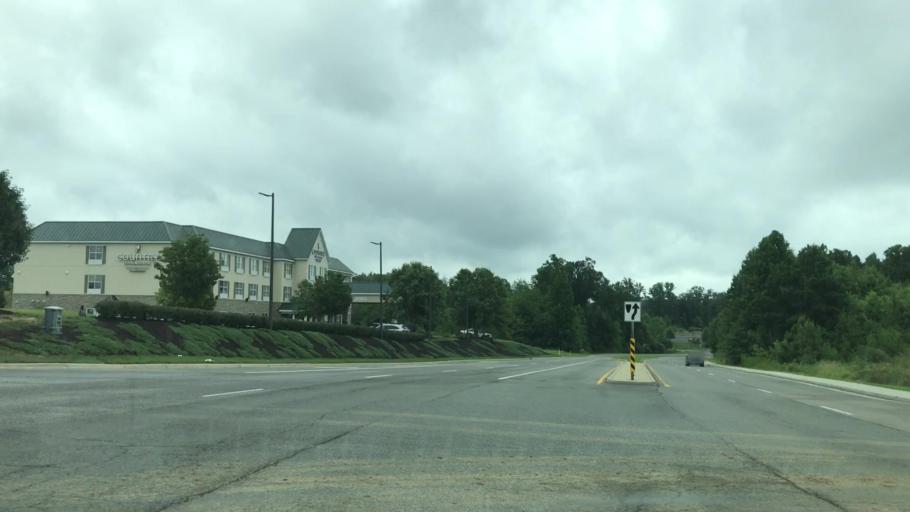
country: US
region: Virginia
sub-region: Hanover County
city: Ashland
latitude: 37.7175
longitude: -77.4512
